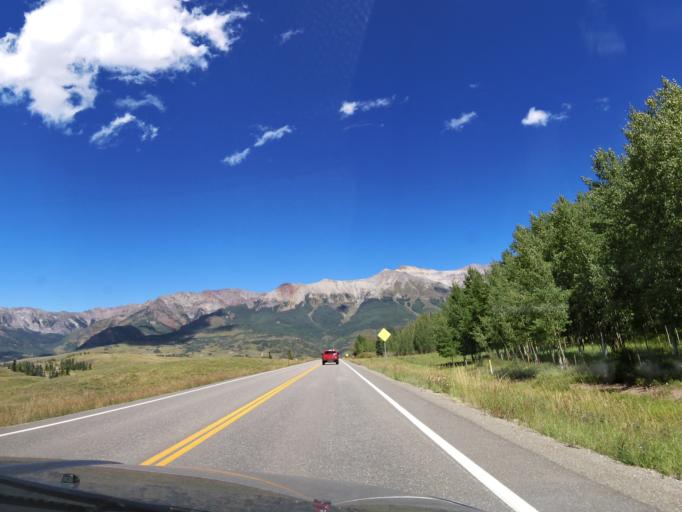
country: US
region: Colorado
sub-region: San Miguel County
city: Mountain Village
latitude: 37.9235
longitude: -107.8834
